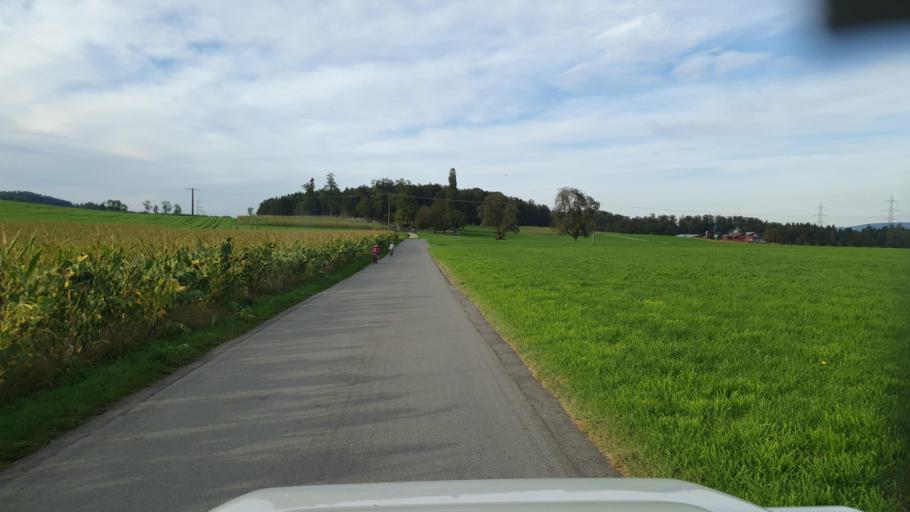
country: CH
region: Aargau
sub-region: Bezirk Muri
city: Auw
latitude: 47.2126
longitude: 8.3717
